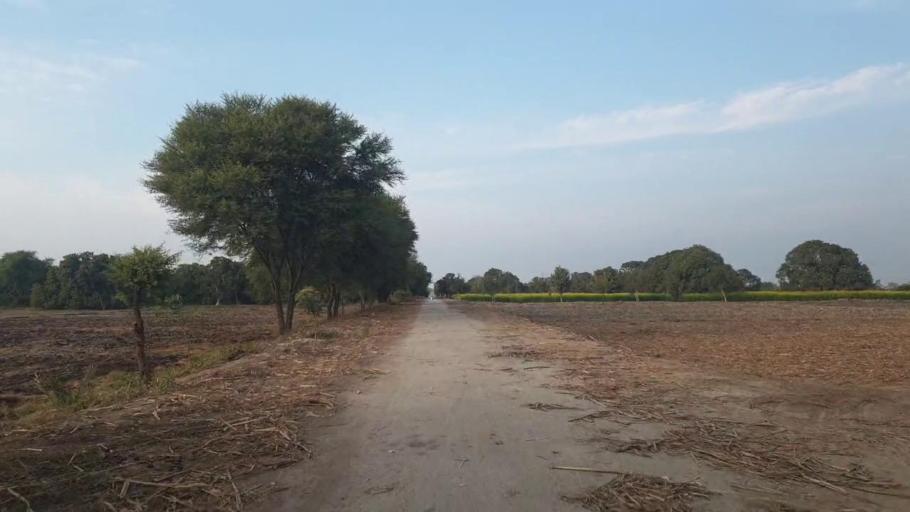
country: PK
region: Sindh
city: Shahpur Chakar
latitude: 26.1098
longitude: 68.5444
